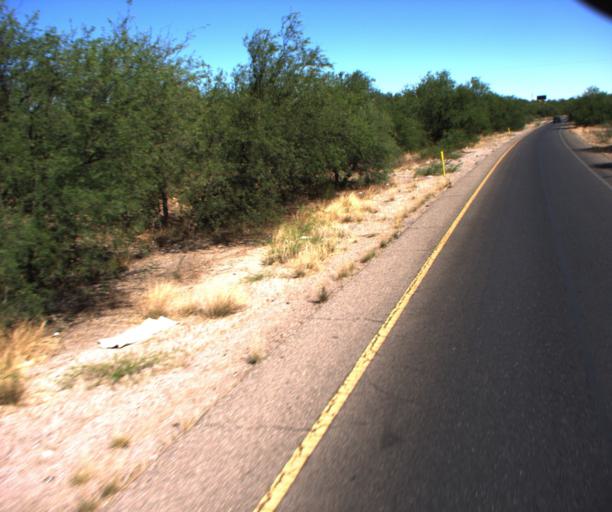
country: US
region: Arizona
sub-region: Santa Cruz County
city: Nogales
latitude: 31.3988
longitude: -110.9597
